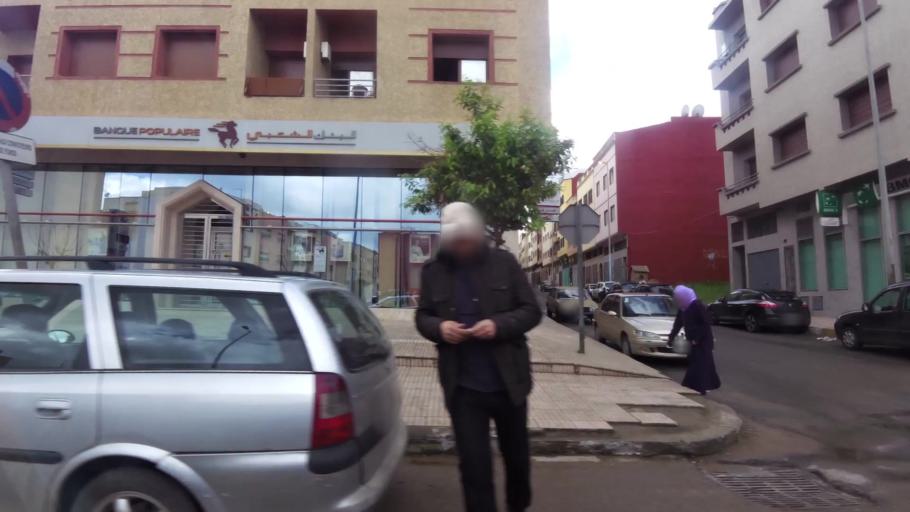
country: MA
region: Grand Casablanca
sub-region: Nouaceur
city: Bouskoura
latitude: 33.5146
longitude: -7.6463
